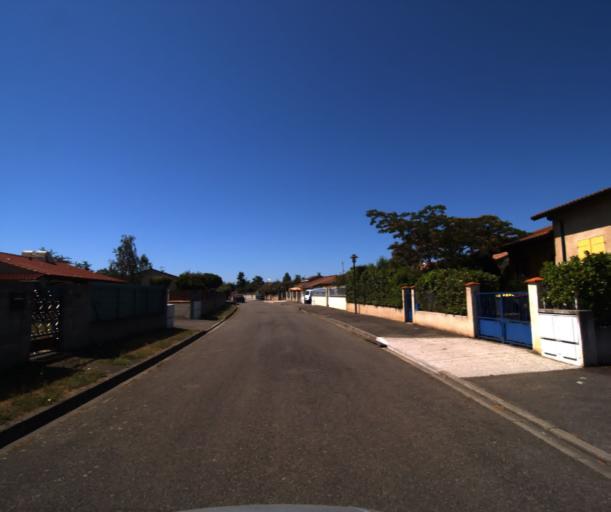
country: FR
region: Midi-Pyrenees
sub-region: Departement de la Haute-Garonne
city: Seysses
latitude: 43.4672
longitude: 1.3161
